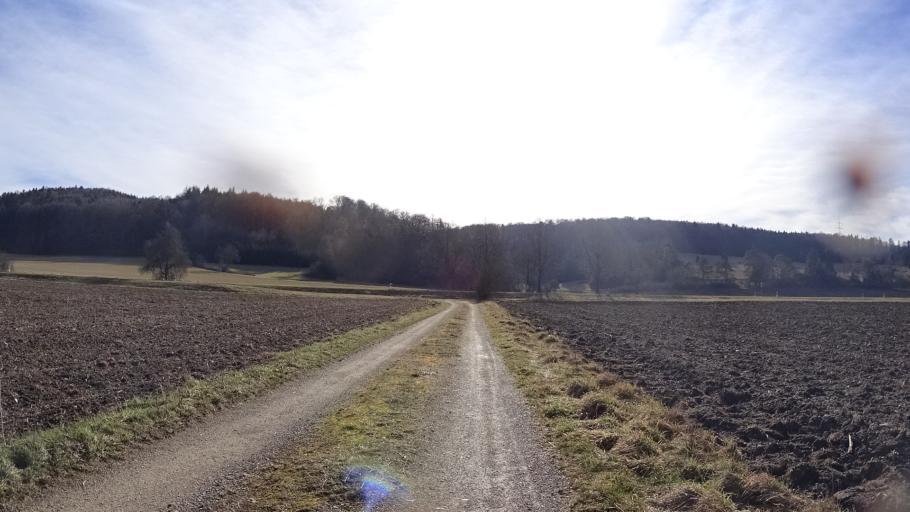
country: DE
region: Bavaria
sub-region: Upper Bavaria
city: Walting
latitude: 48.9019
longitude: 11.2912
